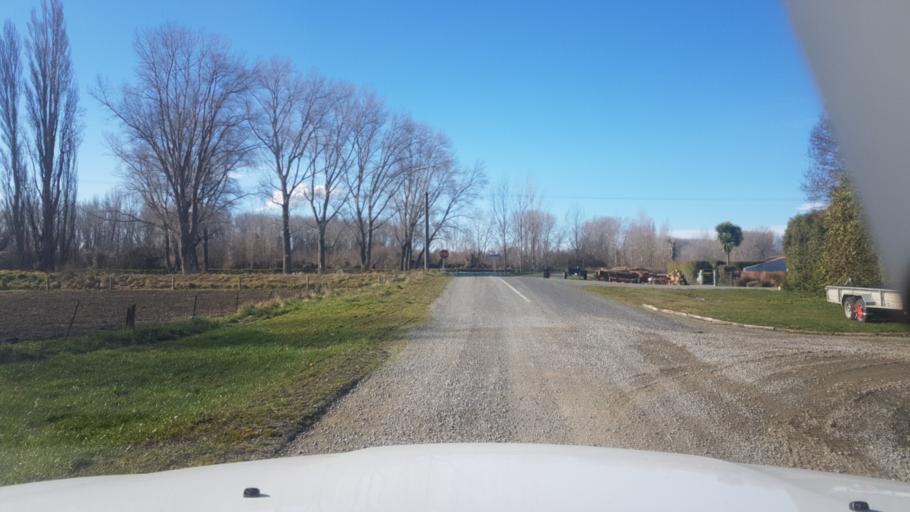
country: NZ
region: Canterbury
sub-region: Timaru District
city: Pleasant Point
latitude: -44.2485
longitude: 171.1177
